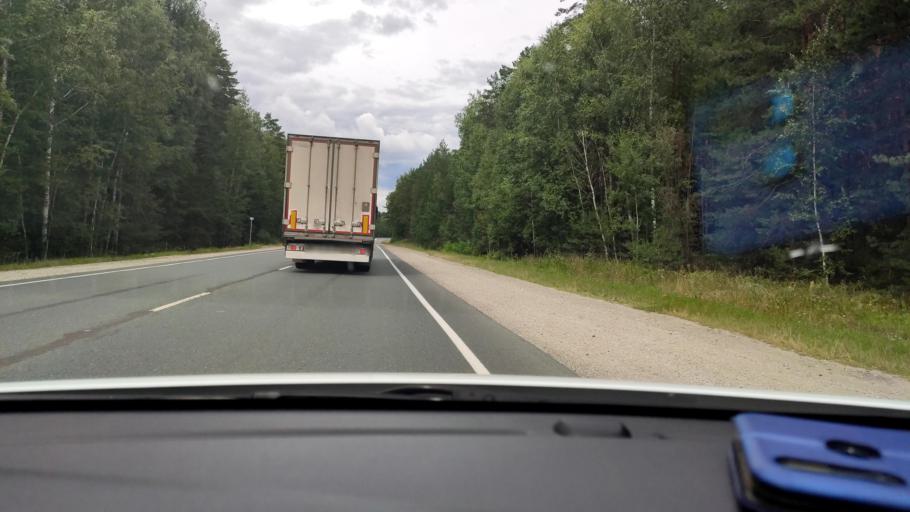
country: RU
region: Mariy-El
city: Pomary
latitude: 56.0024
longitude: 48.3816
